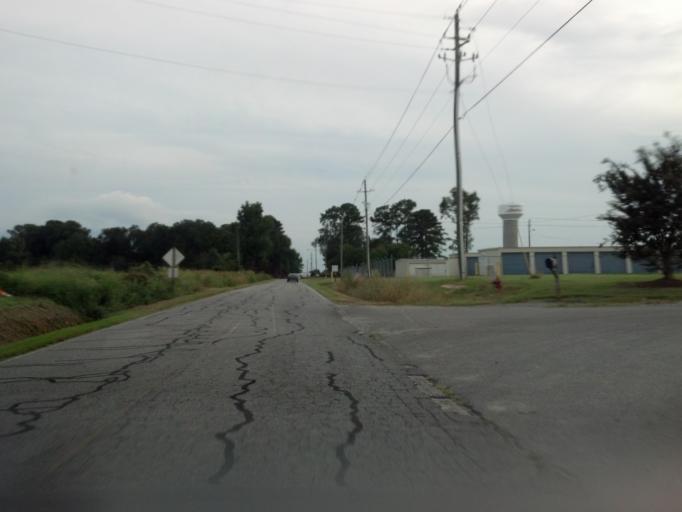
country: US
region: North Carolina
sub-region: Pitt County
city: Ayden
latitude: 35.4887
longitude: -77.4274
